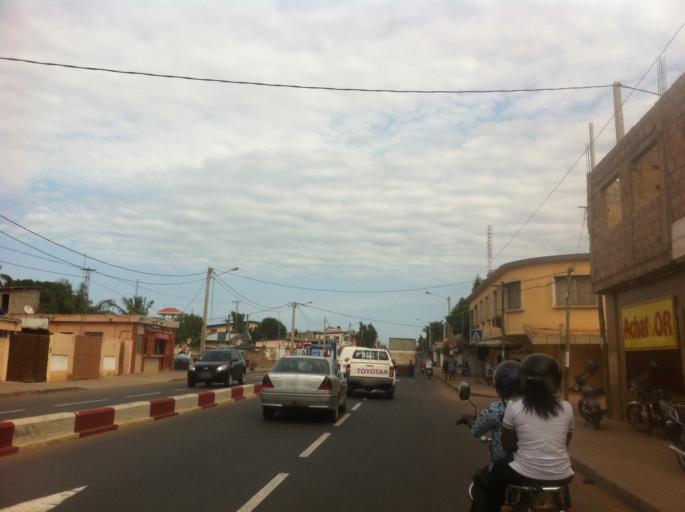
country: TG
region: Maritime
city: Lome
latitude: 6.1480
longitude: 1.2024
